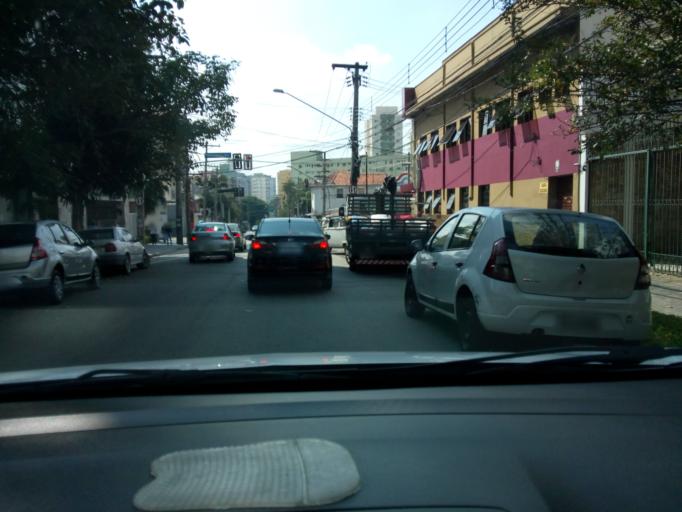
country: BR
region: Sao Paulo
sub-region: Sao Paulo
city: Sao Paulo
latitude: -23.5671
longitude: -46.6338
